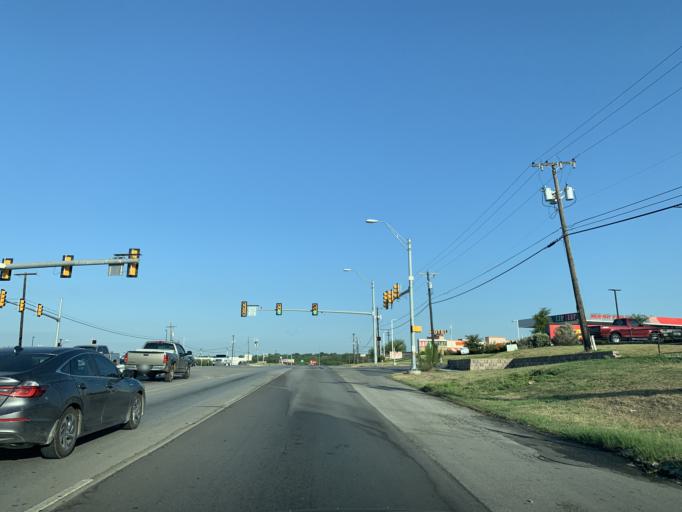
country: US
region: Texas
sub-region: Tarrant County
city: River Oaks
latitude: 32.7838
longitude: -97.3796
